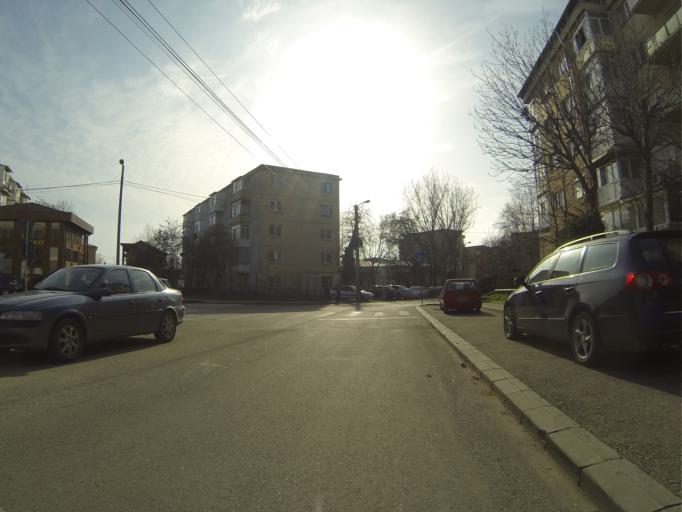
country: RO
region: Dolj
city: Craiova
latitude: 44.3057
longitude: 23.8146
